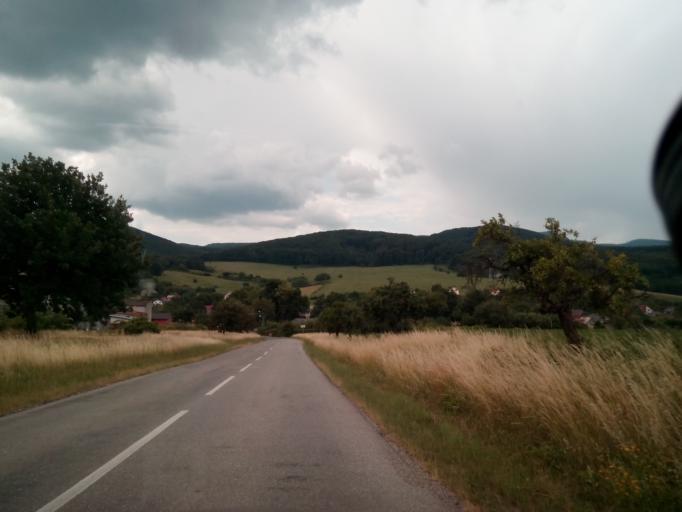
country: SK
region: Kosicky
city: Secovce
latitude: 48.6174
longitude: 21.5230
